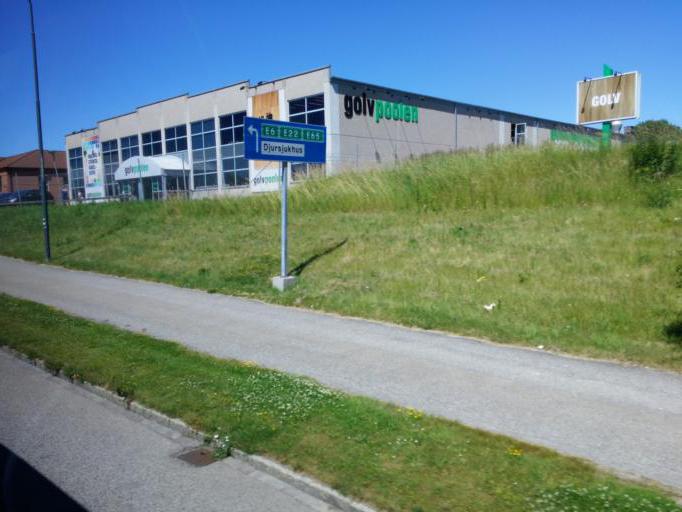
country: SE
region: Skane
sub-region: Malmo
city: Malmoe
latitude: 55.5746
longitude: 13.0485
